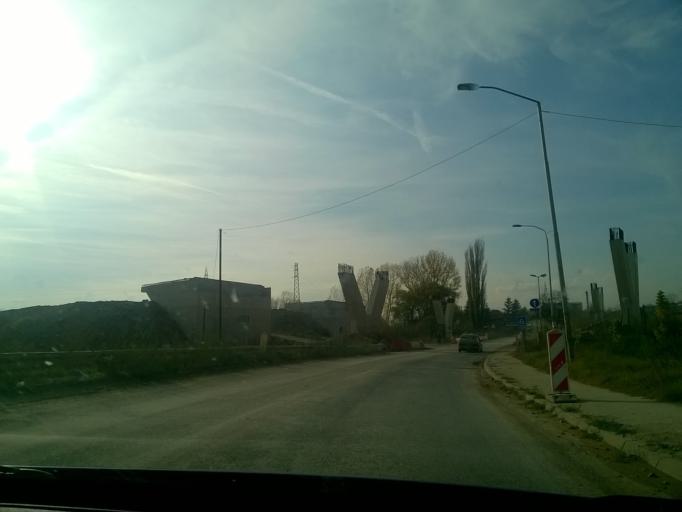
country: RS
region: Central Serbia
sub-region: Pirotski Okrug
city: Pirot
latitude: 43.1585
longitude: 22.5748
